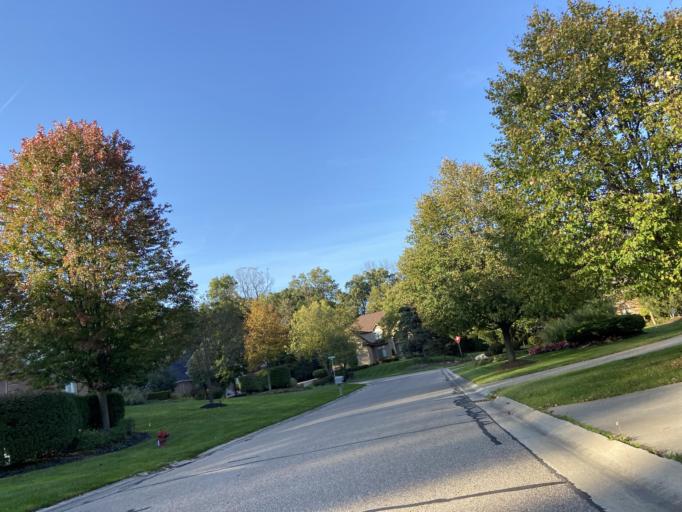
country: US
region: Michigan
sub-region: Oakland County
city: Franklin
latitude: 42.5062
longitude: -83.3239
